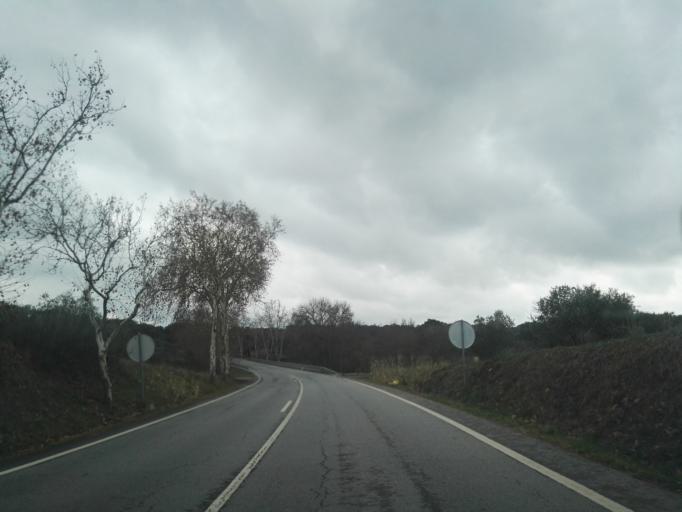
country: PT
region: Portalegre
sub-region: Arronches
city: Arronches
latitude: 39.1285
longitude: -7.2951
